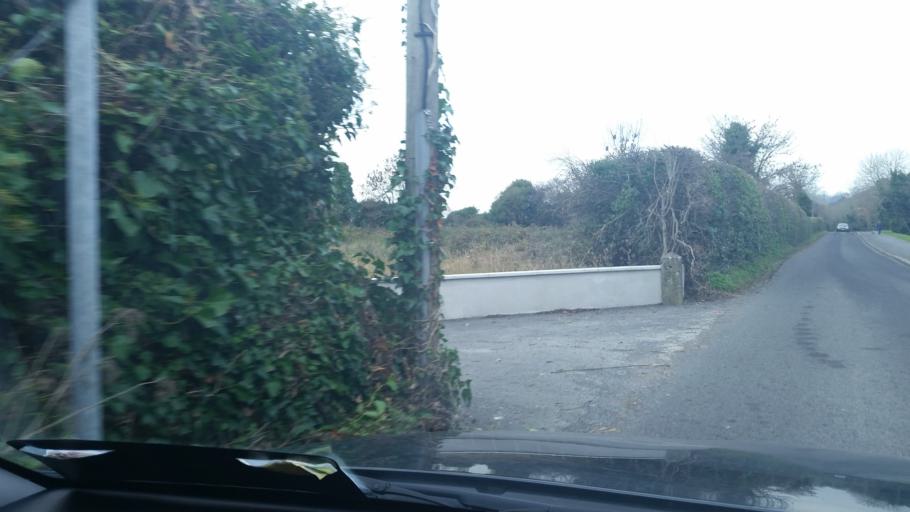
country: IE
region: Leinster
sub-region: Lu
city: Tullyallen
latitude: 53.7211
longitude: -6.4096
